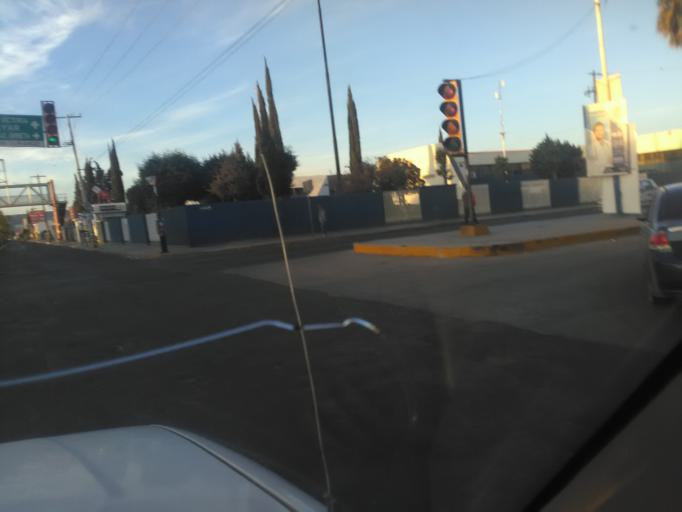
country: MX
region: Durango
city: Victoria de Durango
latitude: 23.9957
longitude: -104.6629
